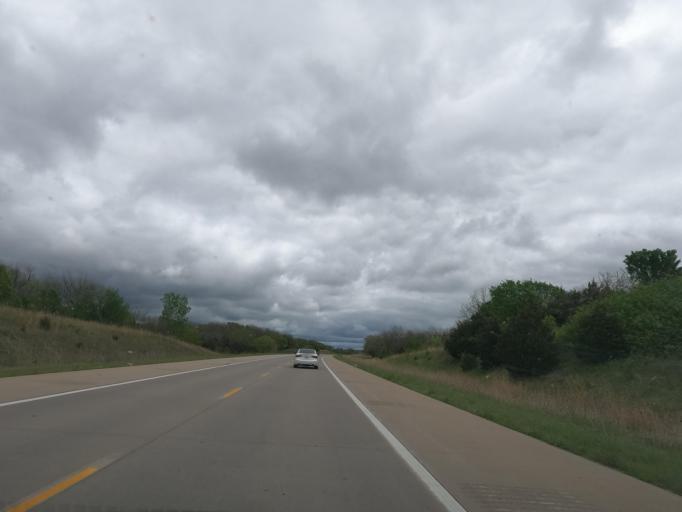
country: US
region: Kansas
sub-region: Wilson County
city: Neodesha
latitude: 37.3547
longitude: -95.6354
